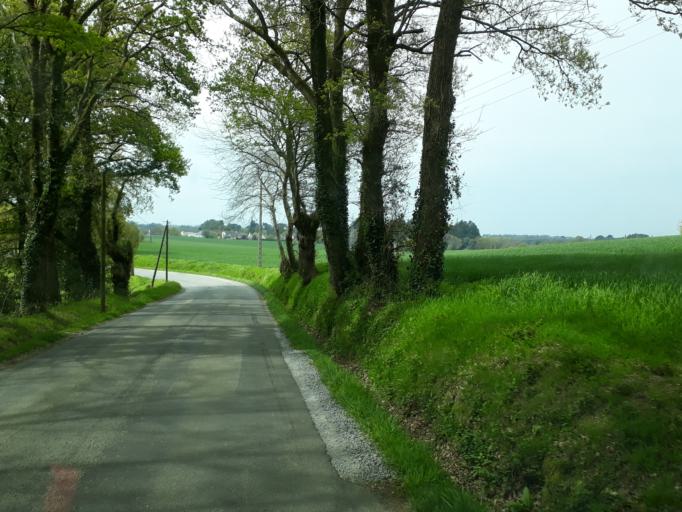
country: FR
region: Brittany
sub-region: Departement du Morbihan
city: Theix
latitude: 47.6467
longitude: -2.6350
